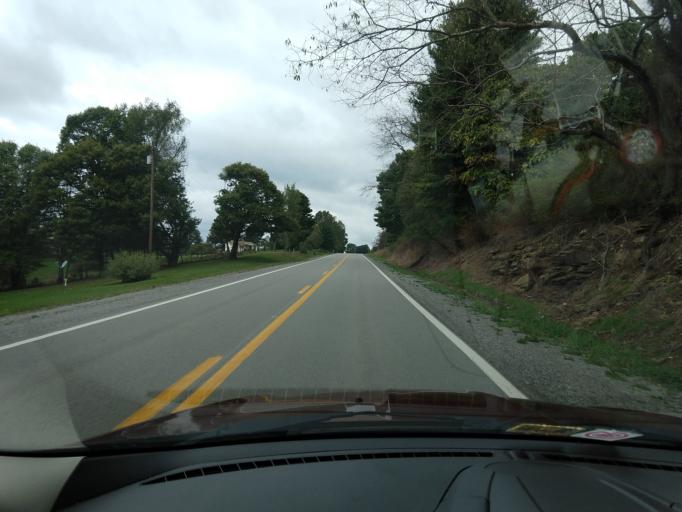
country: US
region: West Virginia
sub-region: Barbour County
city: Belington
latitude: 39.0638
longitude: -79.9739
